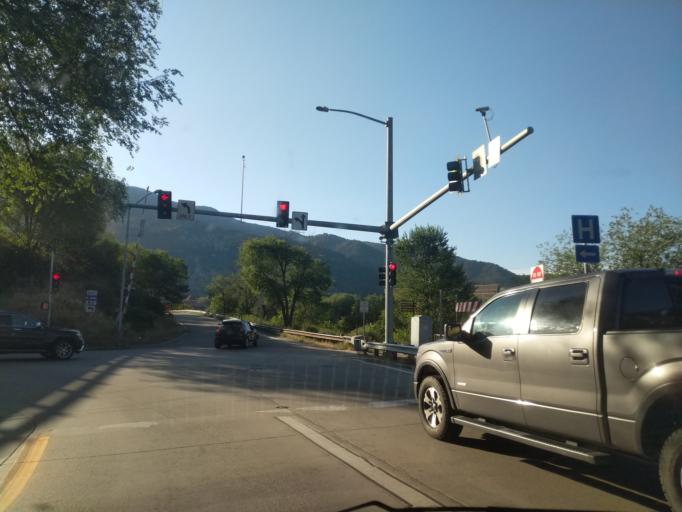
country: US
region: Colorado
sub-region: Garfield County
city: Glenwood Springs
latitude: 39.5494
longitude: -107.3285
